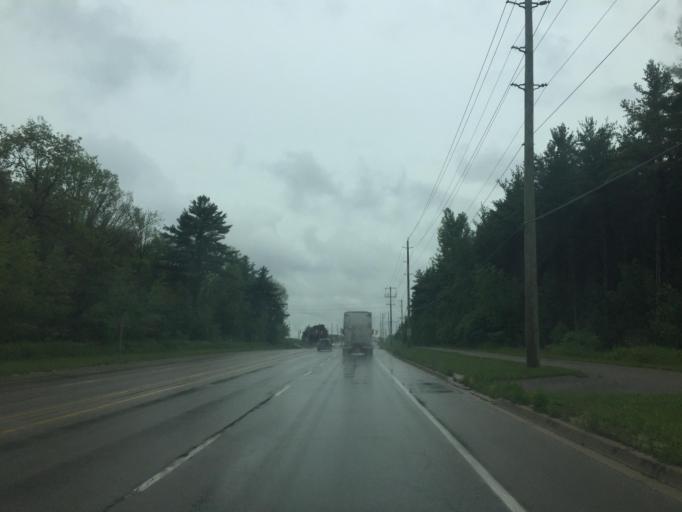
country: CA
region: Ontario
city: Cambridge
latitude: 43.4143
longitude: -80.2803
